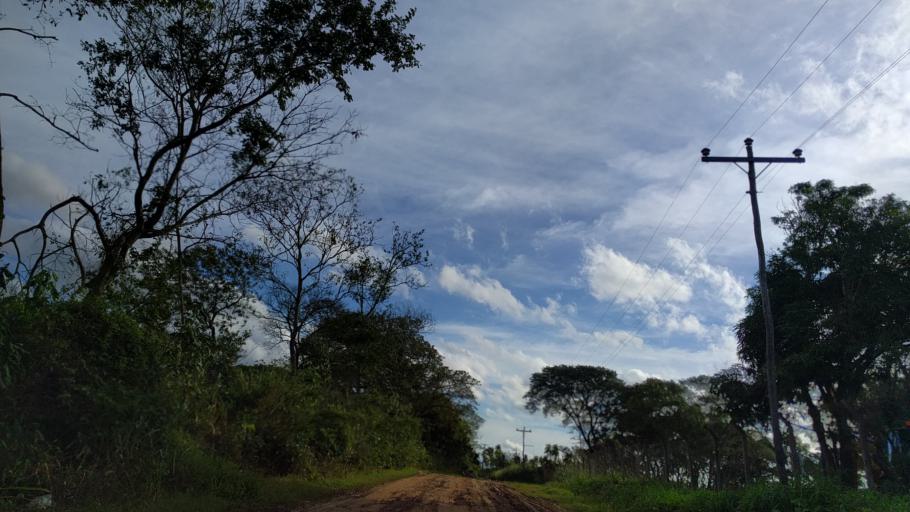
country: BO
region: Santa Cruz
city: Santa Cruz de la Sierra
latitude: -17.8527
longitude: -63.2619
